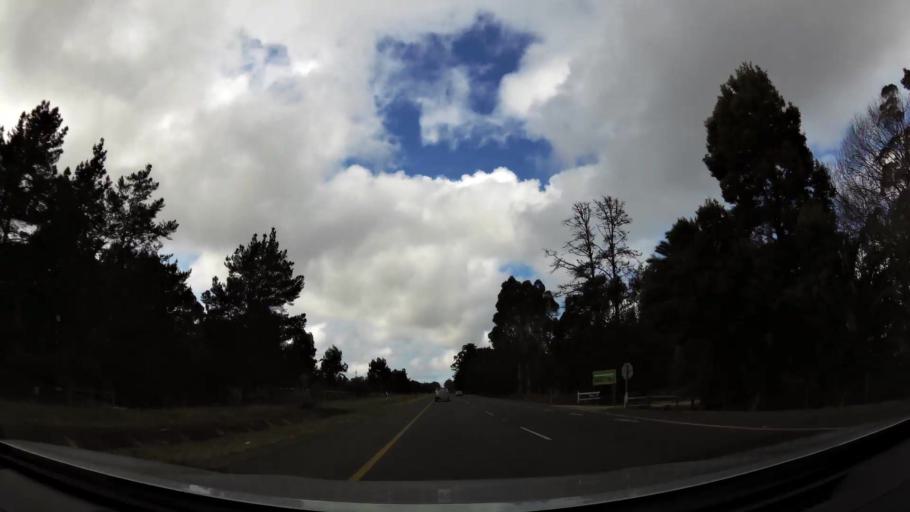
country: ZA
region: Western Cape
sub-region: Eden District Municipality
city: Plettenberg Bay
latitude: -34.0443
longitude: 23.2735
